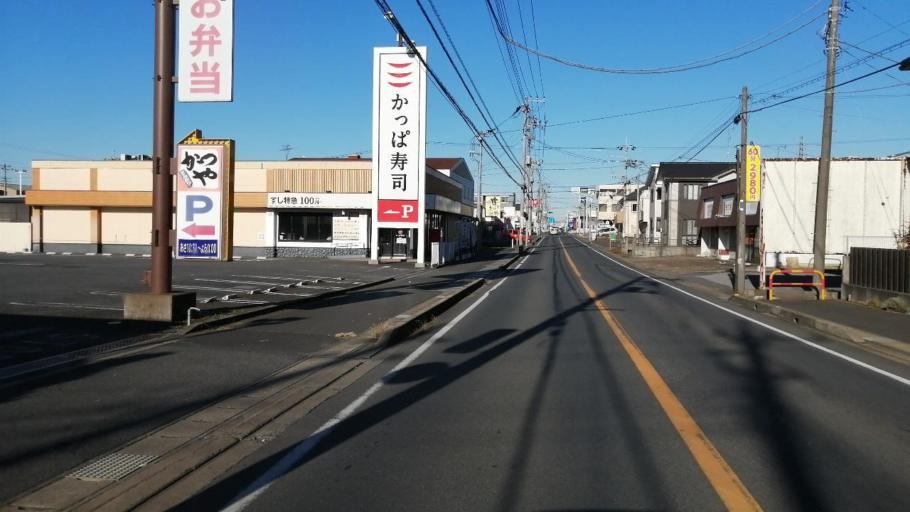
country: JP
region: Chiba
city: Narita
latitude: 35.7404
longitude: 140.3206
